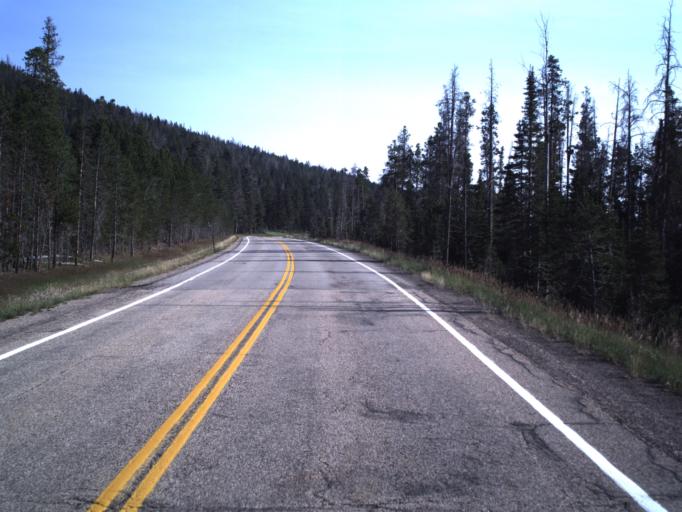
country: US
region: Utah
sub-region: Daggett County
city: Manila
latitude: 40.8160
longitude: -109.4662
